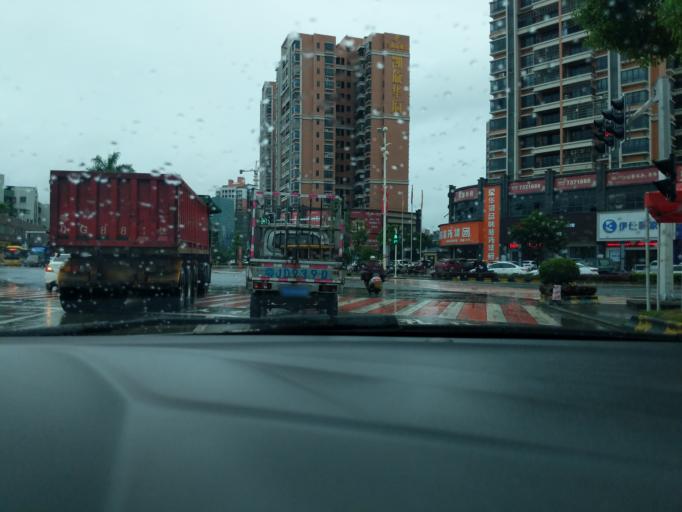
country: CN
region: Guangdong
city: Pingshi
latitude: 22.2023
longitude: 112.3290
